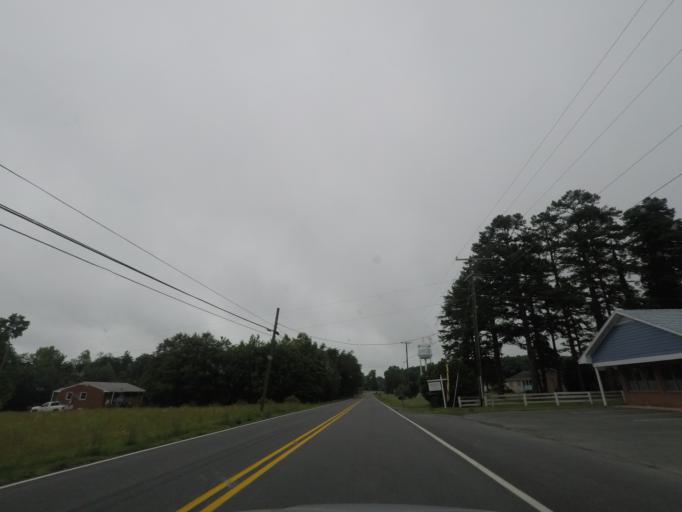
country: US
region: Virginia
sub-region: Fluvanna County
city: Weber City
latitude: 37.7483
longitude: -78.2876
